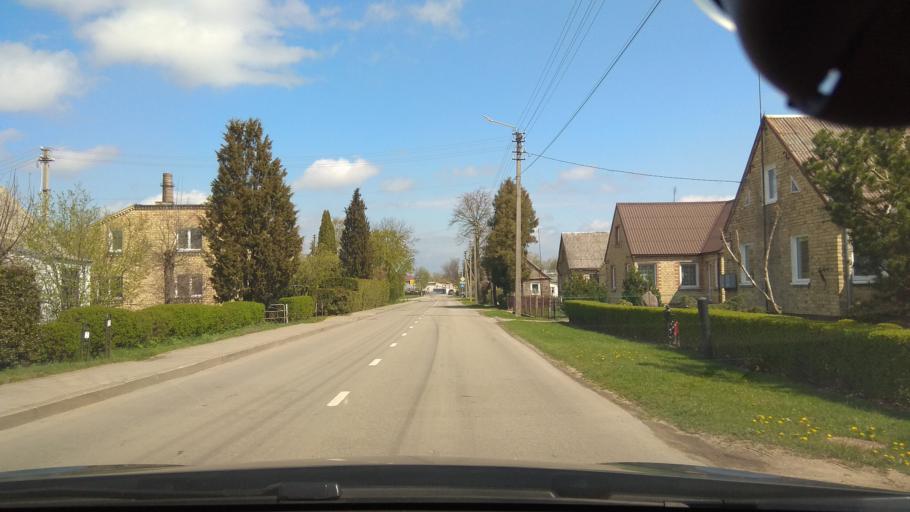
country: LT
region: Siauliu apskritis
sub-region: Joniskis
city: Joniskis
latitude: 56.2405
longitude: 23.6272
